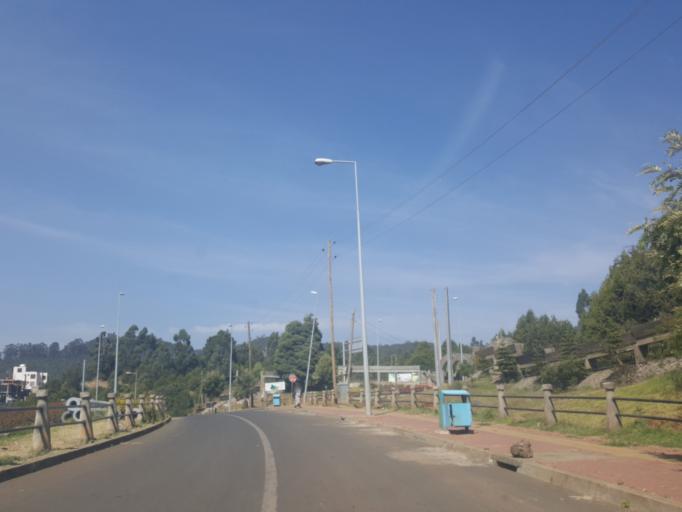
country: ET
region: Adis Abeba
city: Addis Ababa
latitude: 9.0704
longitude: 38.7224
